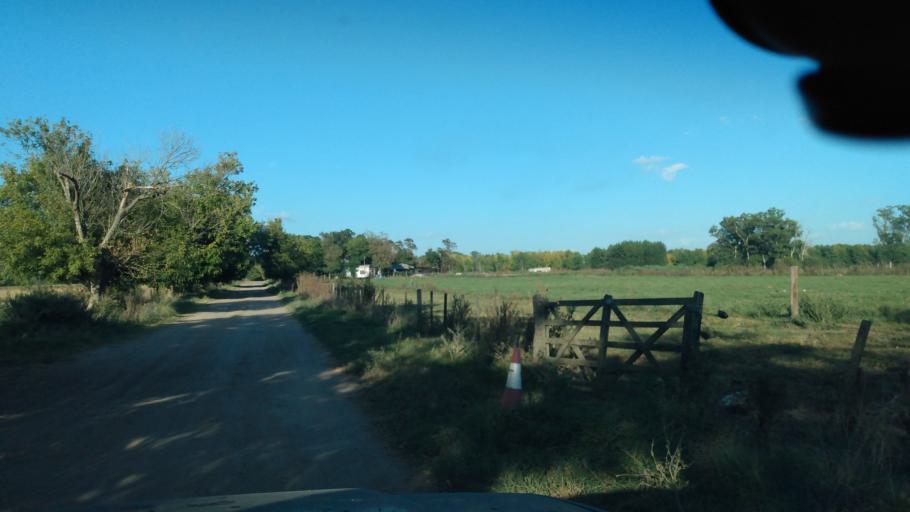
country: AR
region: Buenos Aires
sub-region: Partido de Lujan
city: Lujan
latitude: -34.5877
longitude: -59.0692
